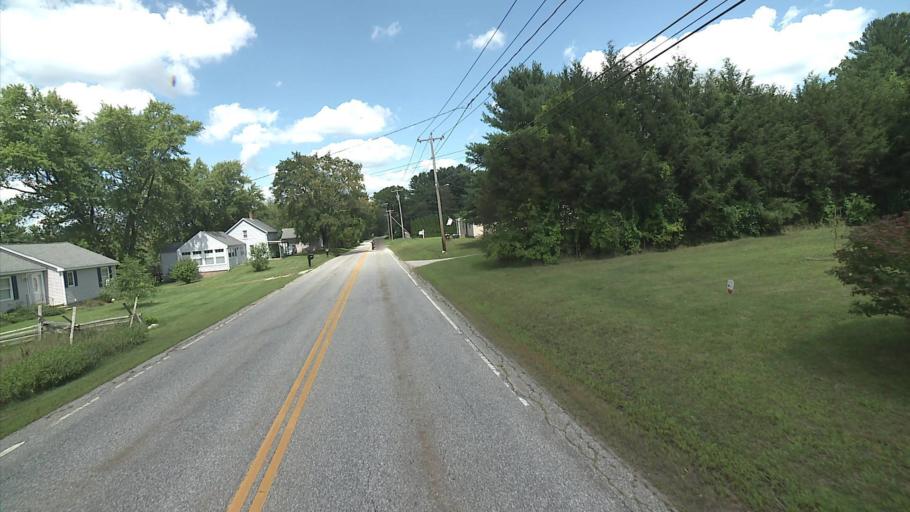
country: US
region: Connecticut
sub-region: Windham County
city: Windham
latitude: 41.7251
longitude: -72.1671
